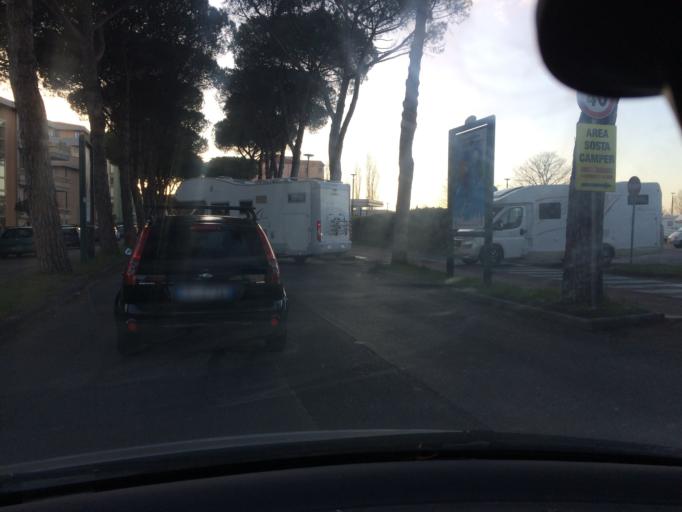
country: IT
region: Tuscany
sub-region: Province of Pisa
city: Pisa
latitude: 43.7209
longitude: 10.4208
